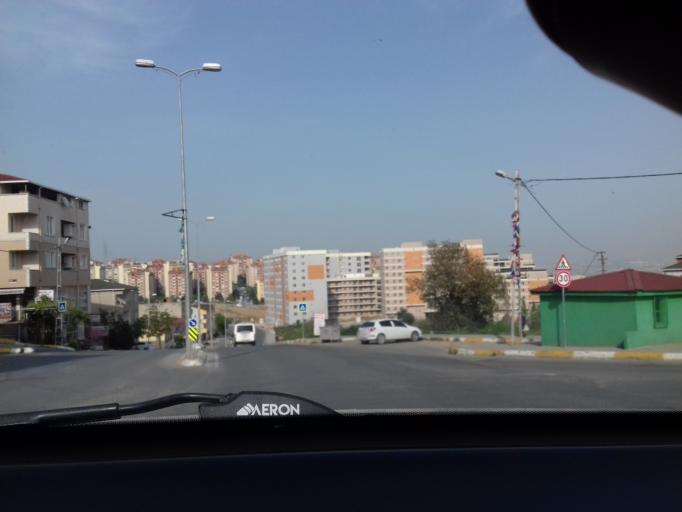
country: TR
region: Istanbul
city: Pendik
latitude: 40.9048
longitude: 29.2698
